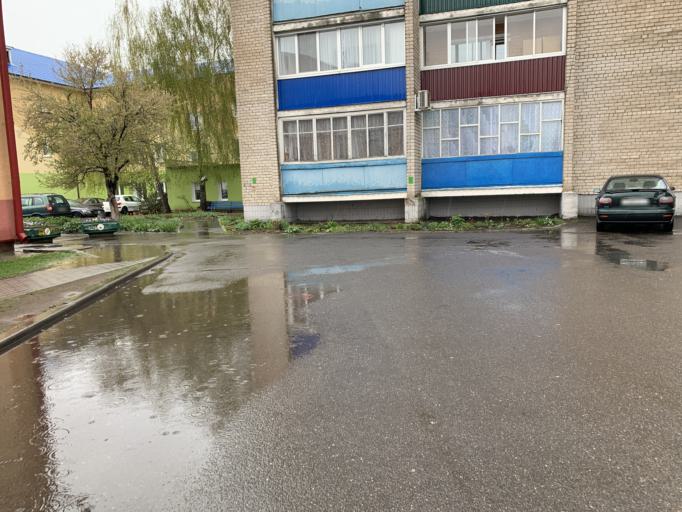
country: BY
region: Minsk
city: Klyetsk
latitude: 53.0677
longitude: 26.6341
